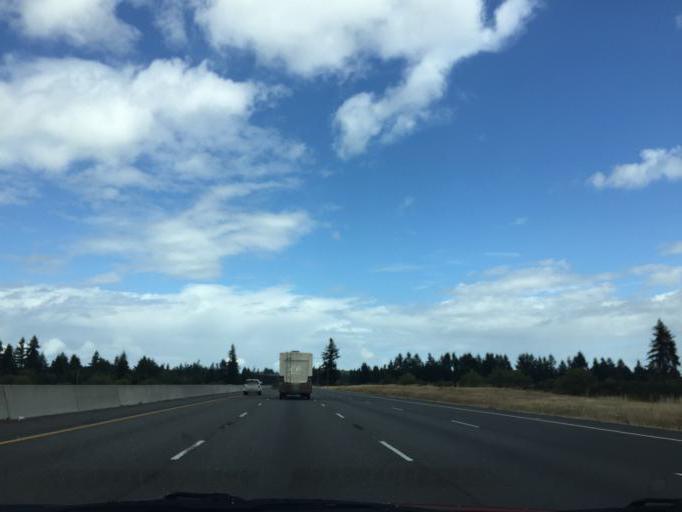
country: US
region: Washington
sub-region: Thurston County
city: Grand Mound
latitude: 46.8422
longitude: -122.9833
